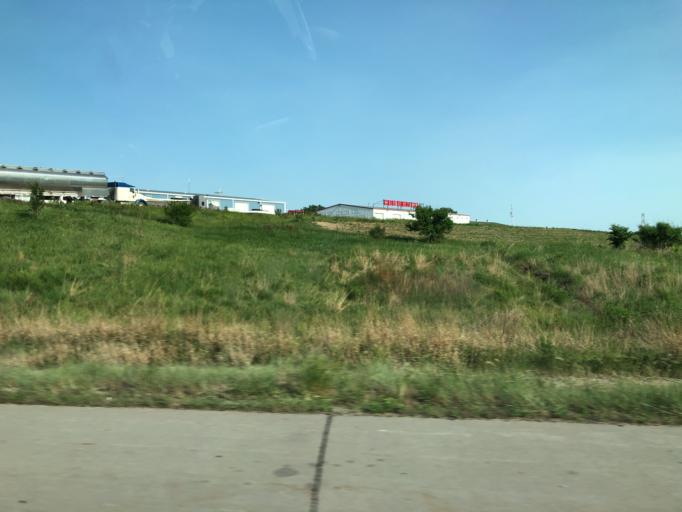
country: US
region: Nebraska
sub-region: Sarpy County
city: Gretna
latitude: 41.0907
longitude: -96.2609
